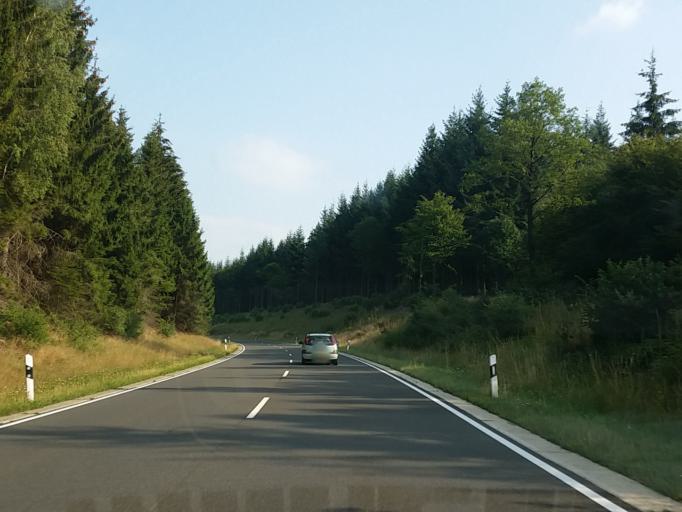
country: DE
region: Rheinland-Pfalz
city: Reinsfeld
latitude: 49.6984
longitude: 6.8531
